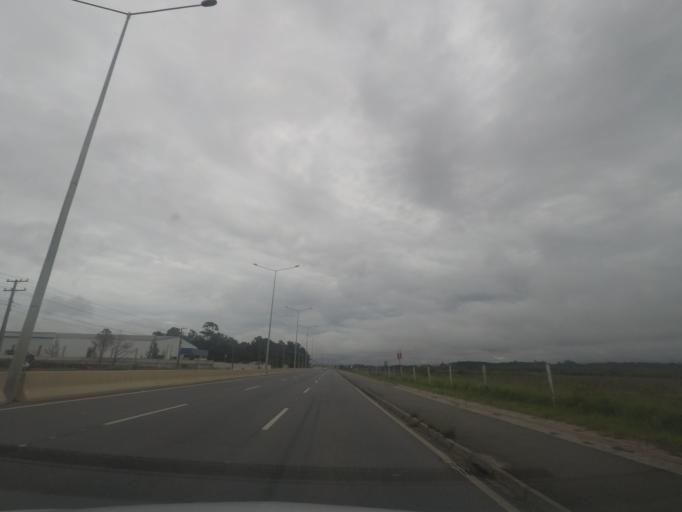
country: BR
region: Parana
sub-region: Pinhais
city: Pinhais
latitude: -25.4475
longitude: -49.1332
